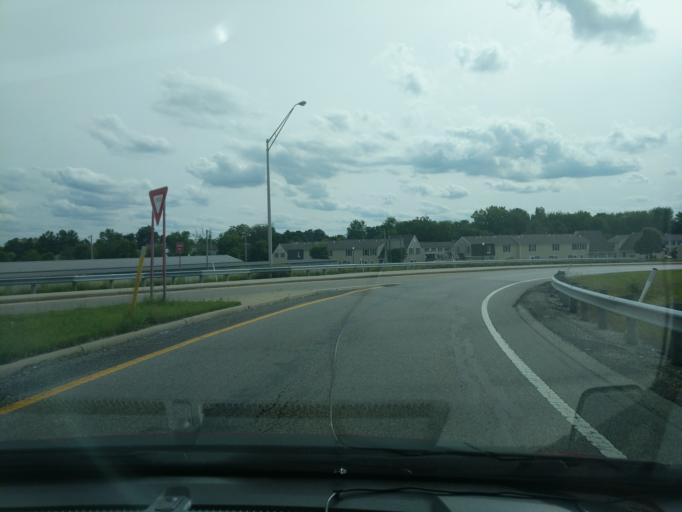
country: US
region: Ohio
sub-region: Union County
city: Marysville
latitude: 40.2530
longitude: -83.3735
